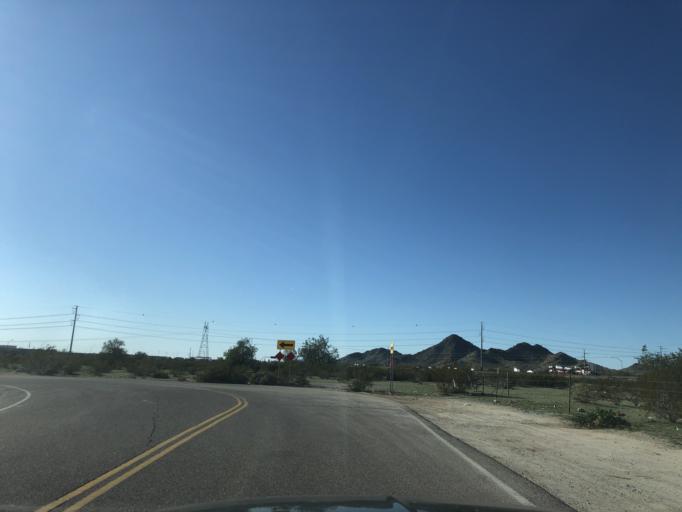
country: US
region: Arizona
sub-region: Maricopa County
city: Buckeye
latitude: 33.4301
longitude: -112.5948
